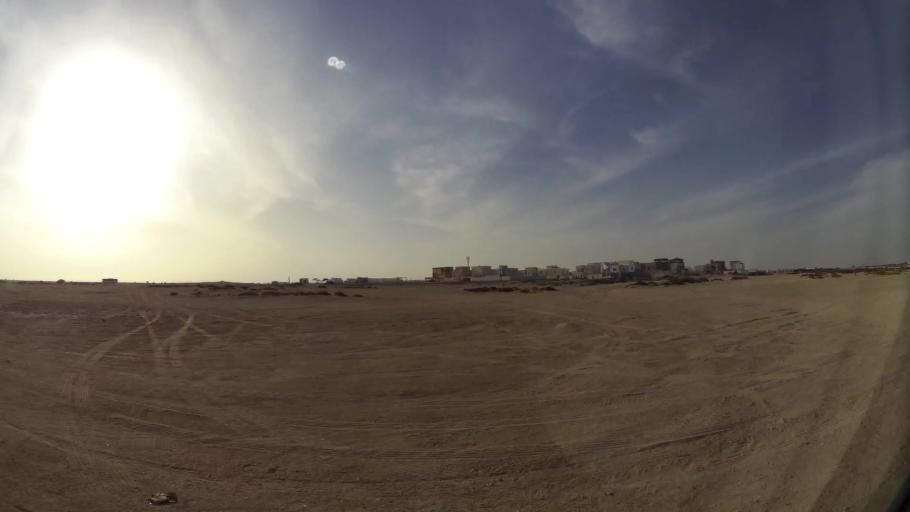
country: QA
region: Al Wakrah
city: Al Wakrah
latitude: 25.1388
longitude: 51.6178
